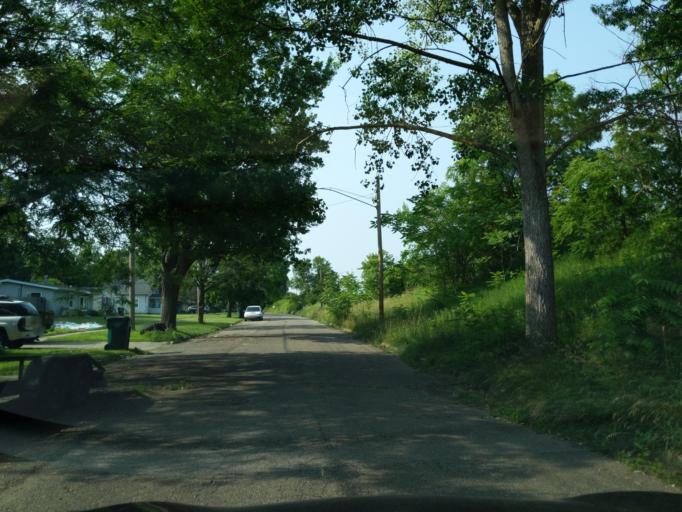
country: US
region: Michigan
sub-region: Ingham County
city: Lansing
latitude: 42.7203
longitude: -84.5226
